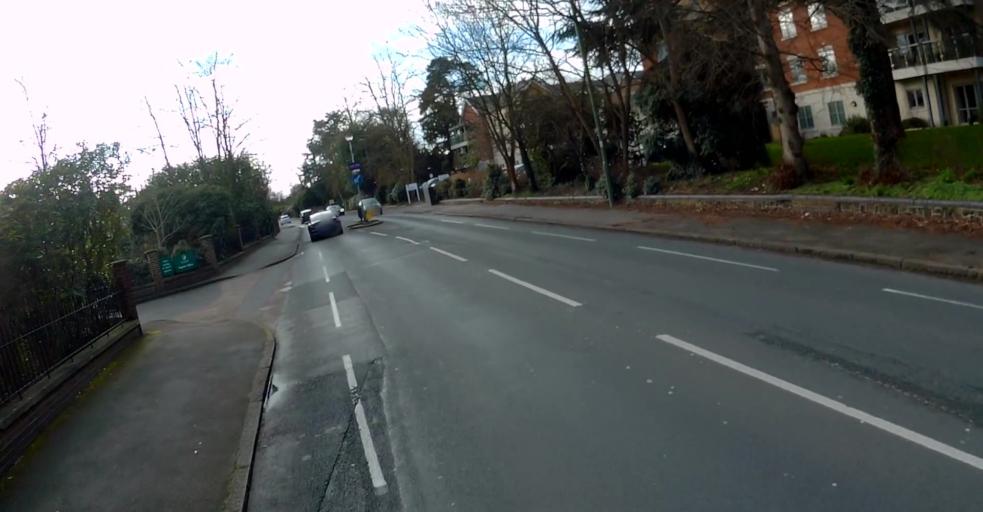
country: GB
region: England
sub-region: Surrey
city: Walton-on-Thames
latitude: 51.3791
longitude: -0.4334
